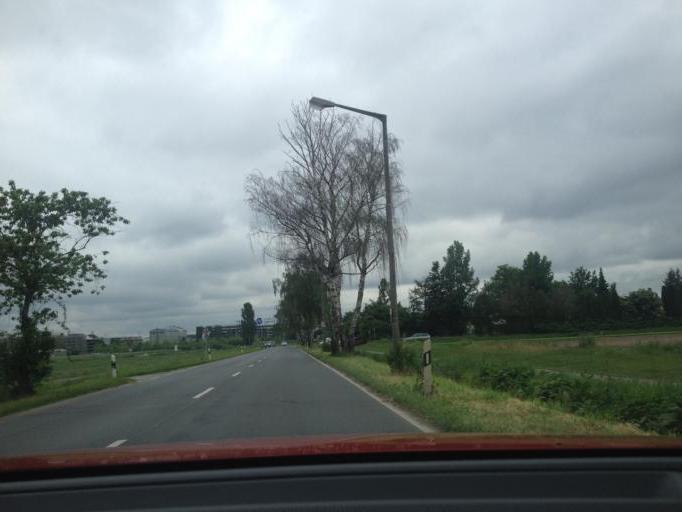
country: DE
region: Bavaria
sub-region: Regierungsbezirk Mittelfranken
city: Nuernberg
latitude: 49.4869
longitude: 11.0822
